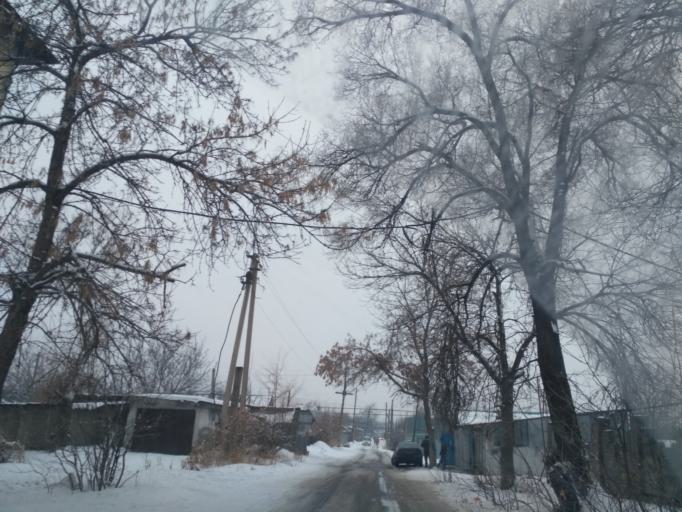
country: KZ
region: Almaty Oblysy
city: Burunday
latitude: 43.1600
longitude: 76.4114
